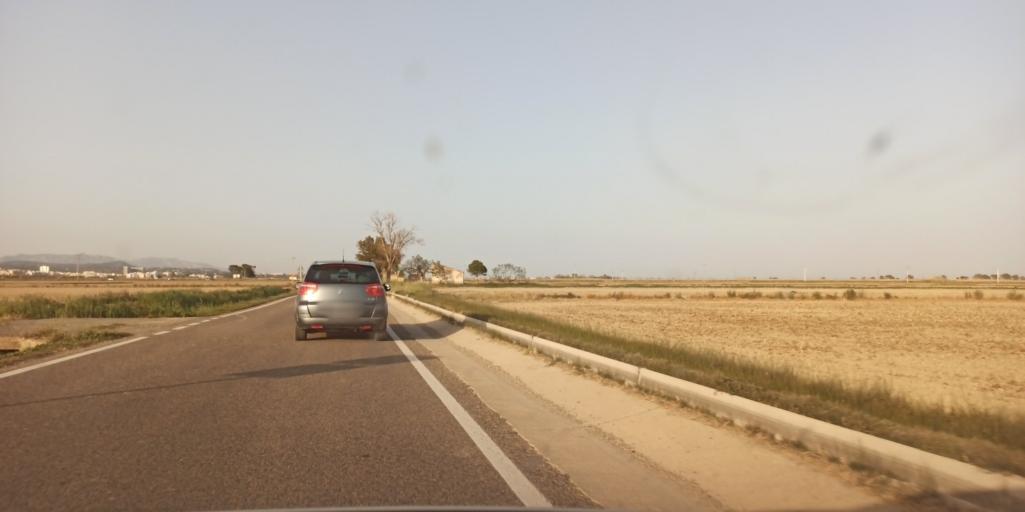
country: ES
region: Catalonia
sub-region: Provincia de Tarragona
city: L'Ampolla
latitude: 40.7876
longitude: 0.6937
